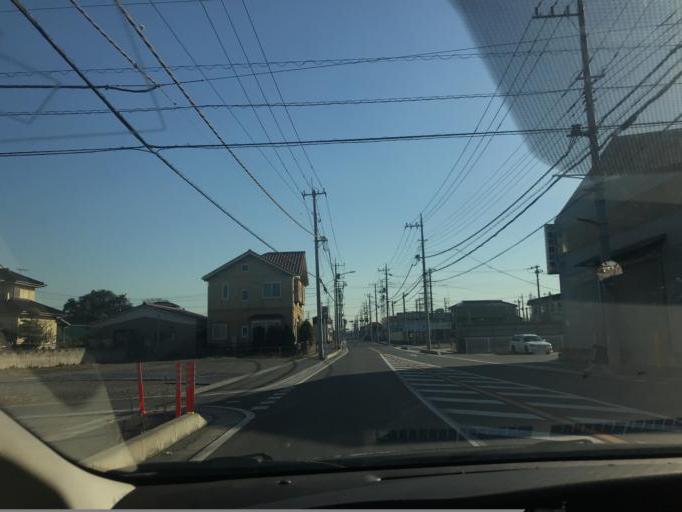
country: JP
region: Saitama
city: Yashio-shi
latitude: 35.8332
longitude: 139.8386
